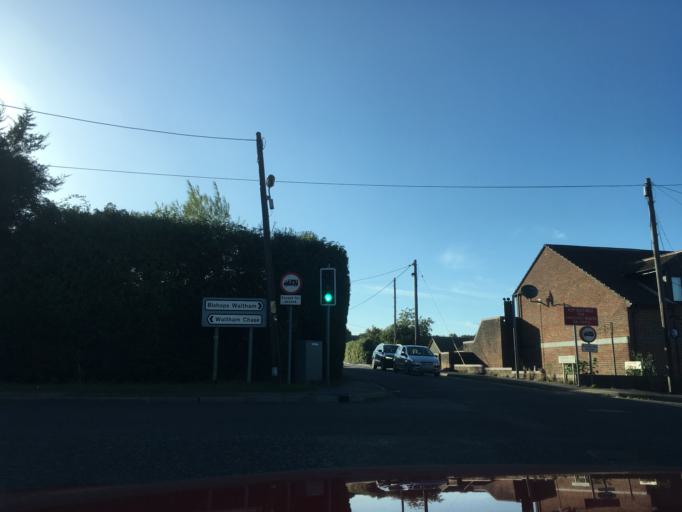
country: GB
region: England
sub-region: Hampshire
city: Bishops Waltham
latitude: 50.9355
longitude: -1.2007
